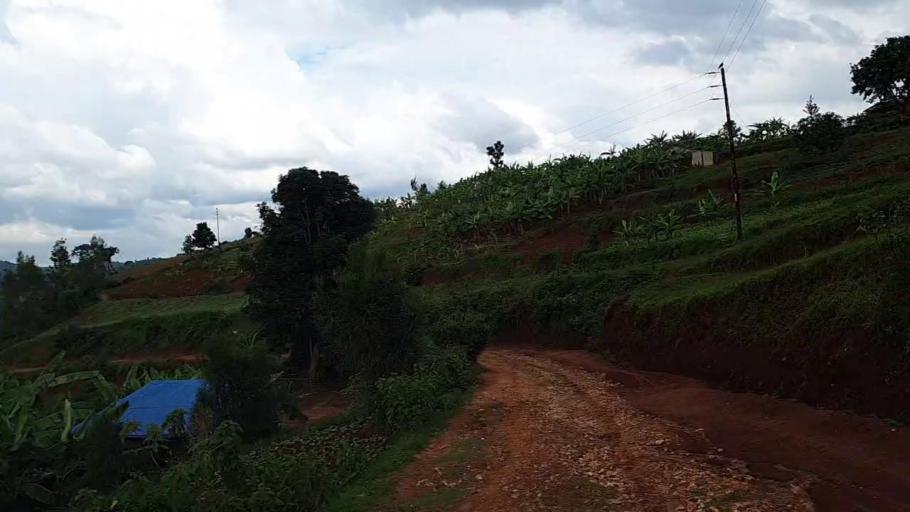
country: RW
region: Southern Province
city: Gikongoro
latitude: -2.4209
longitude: 29.6535
